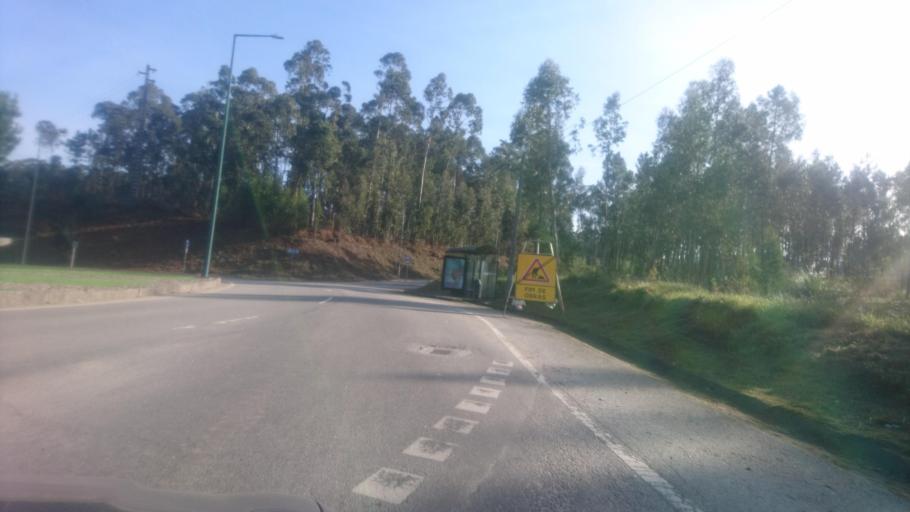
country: PT
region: Aveiro
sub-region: Santa Maria da Feira
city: Rio Meao
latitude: 40.9267
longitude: -8.5754
